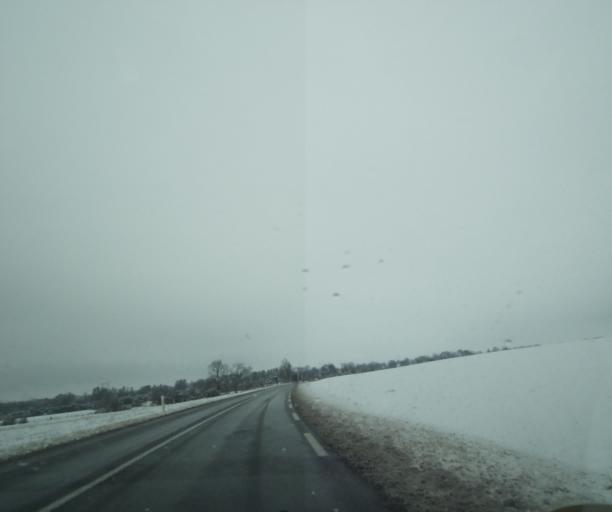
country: FR
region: Champagne-Ardenne
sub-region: Departement de la Haute-Marne
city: Montier-en-Der
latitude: 48.5112
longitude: 4.8026
